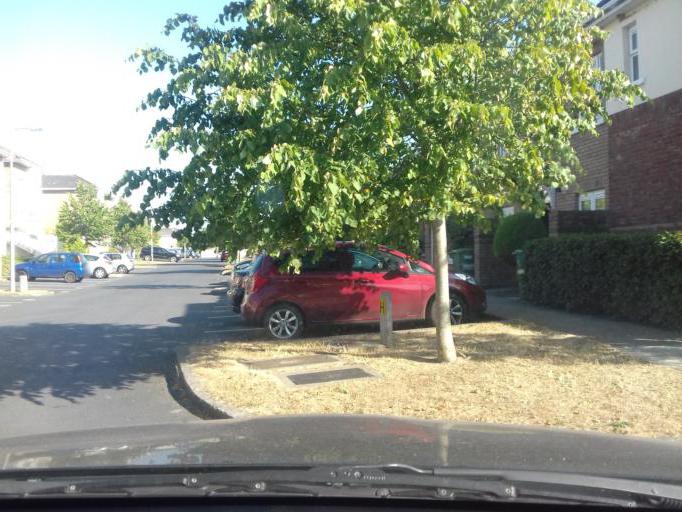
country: IE
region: Leinster
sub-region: Fingal County
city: Blanchardstown
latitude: 53.4228
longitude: -6.3948
